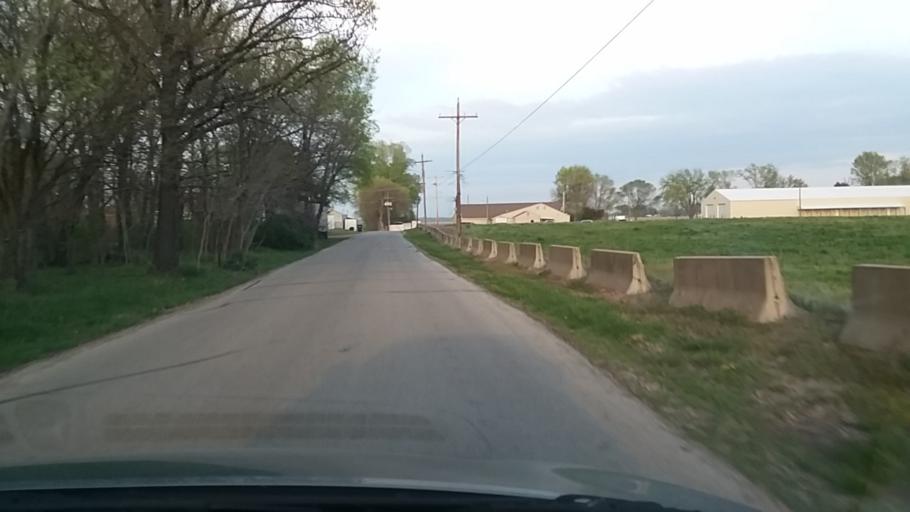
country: US
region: Kansas
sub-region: Douglas County
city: Lawrence
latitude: 38.9751
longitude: -95.2162
